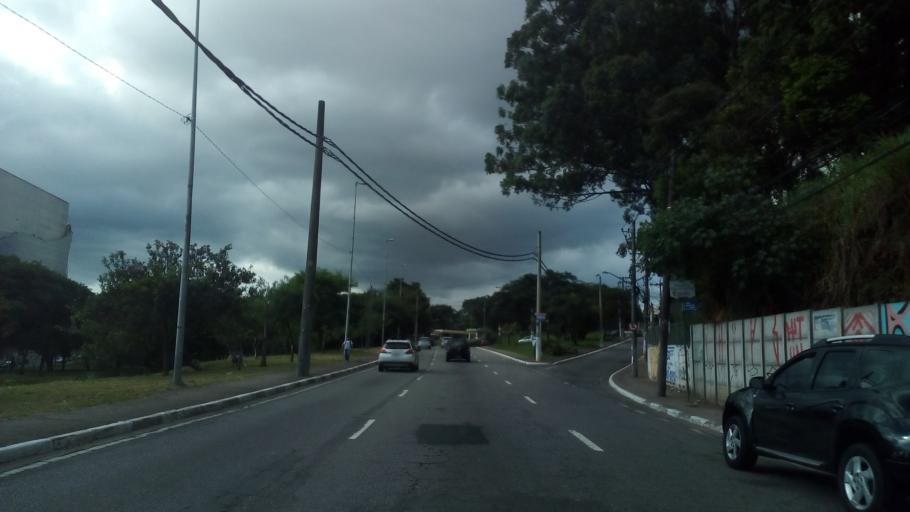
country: BR
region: Sao Paulo
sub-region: Guarulhos
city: Guarulhos
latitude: -23.4443
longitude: -46.5378
